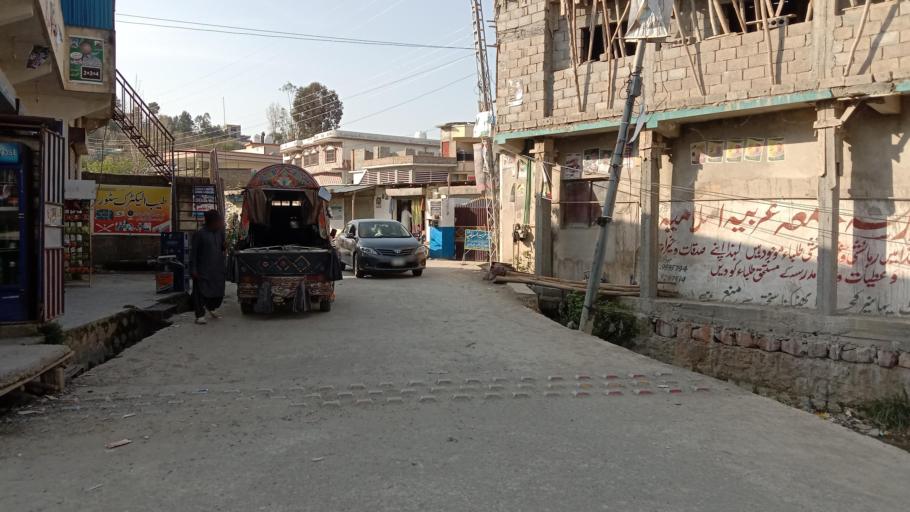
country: PK
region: Khyber Pakhtunkhwa
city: Abbottabad
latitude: 34.2024
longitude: 73.2250
